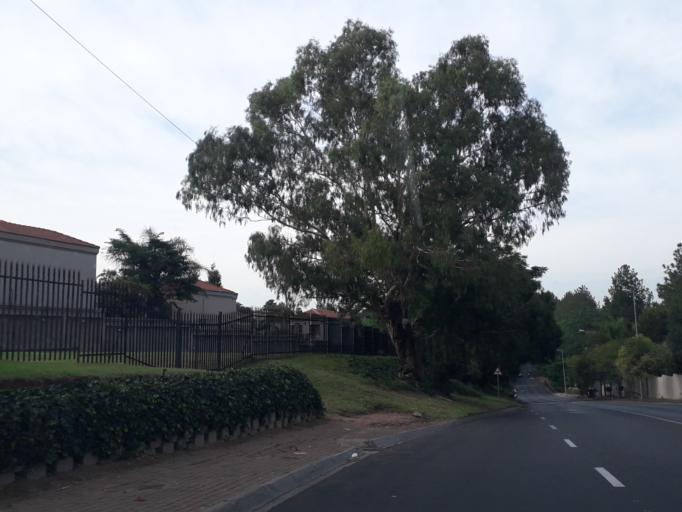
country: ZA
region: Gauteng
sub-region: City of Johannesburg Metropolitan Municipality
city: Johannesburg
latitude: -26.0804
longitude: 28.0430
